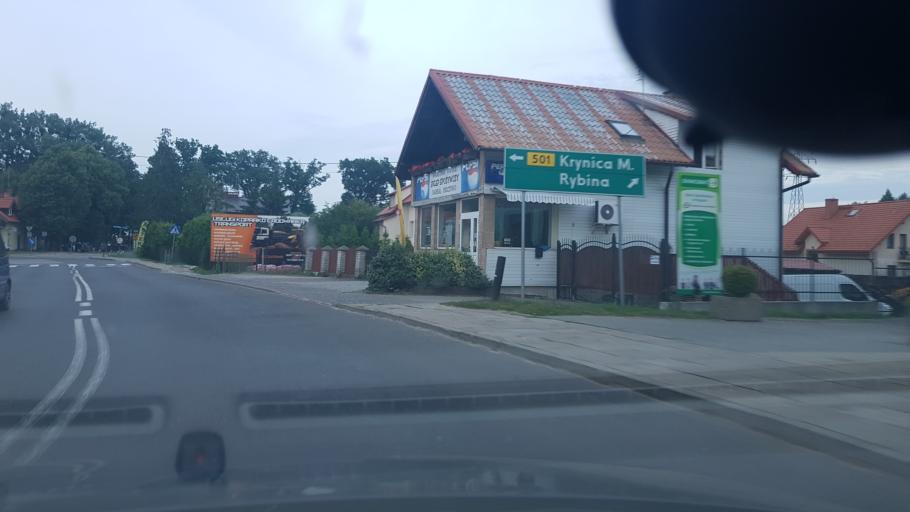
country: PL
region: Pomeranian Voivodeship
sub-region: Powiat nowodworski
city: Sztutowo
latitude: 54.3258
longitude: 19.1777
